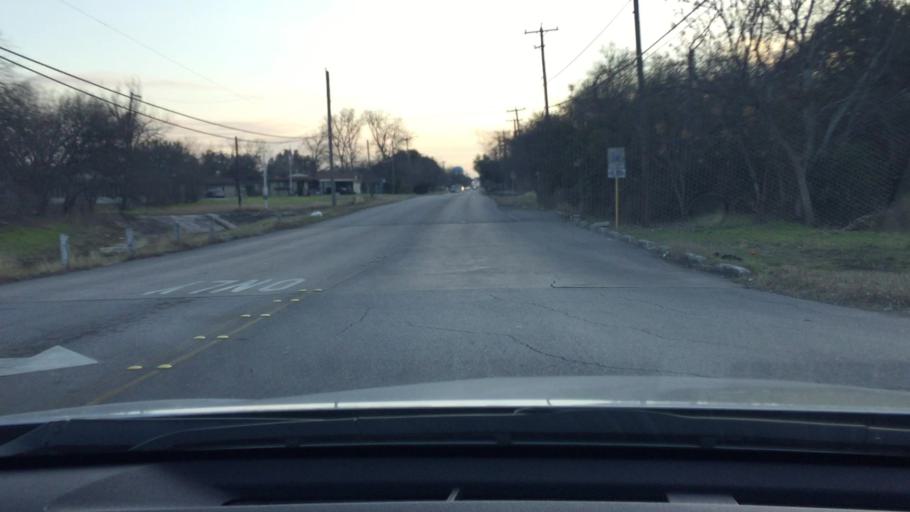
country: US
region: Texas
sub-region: Bexar County
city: Terrell Hills
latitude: 29.4957
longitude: -98.4245
